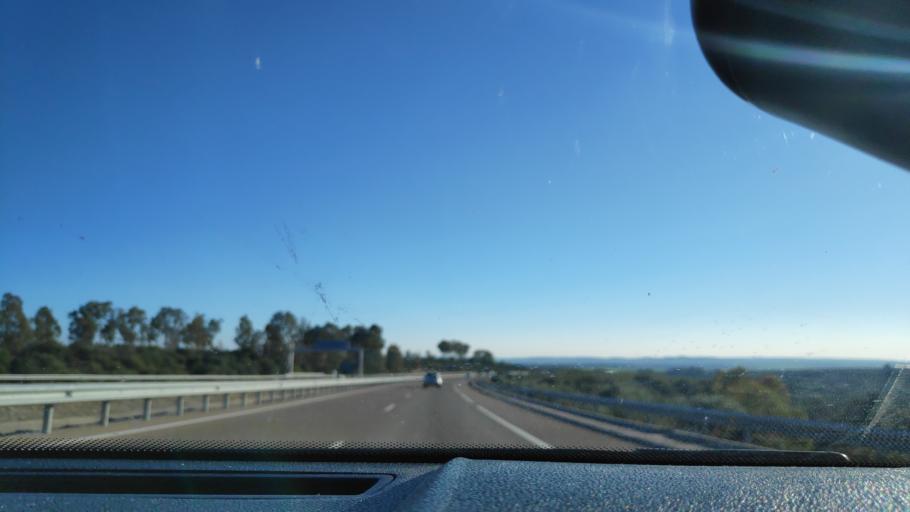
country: ES
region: Andalusia
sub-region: Provincia de Sevilla
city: Guillena
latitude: 37.5656
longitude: -6.1035
